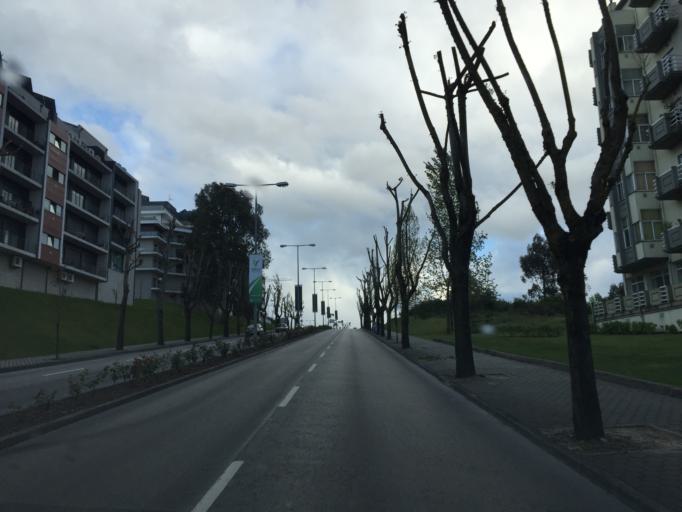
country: PT
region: Viseu
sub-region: Viseu
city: Viseu
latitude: 40.6581
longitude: -7.9232
